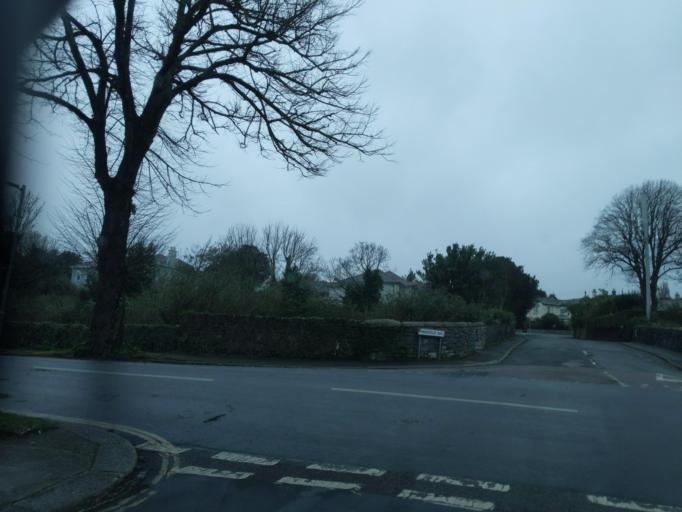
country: GB
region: England
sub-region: Plymouth
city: Plymouth
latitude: 50.3776
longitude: -4.1581
